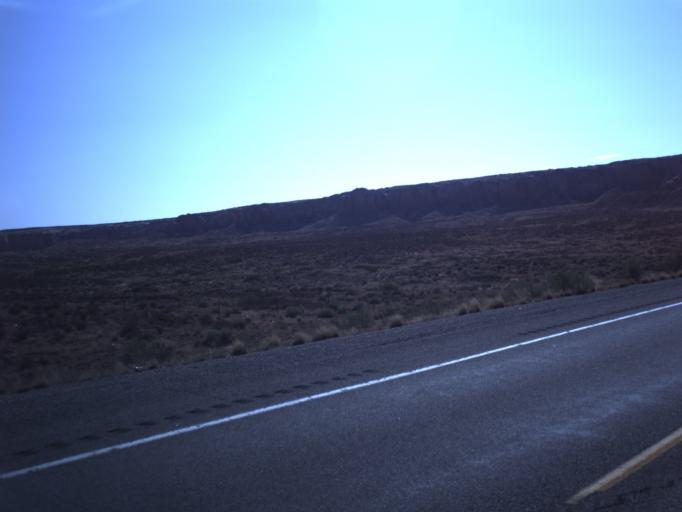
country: US
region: Utah
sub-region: San Juan County
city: Blanding
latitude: 37.2460
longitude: -109.6085
